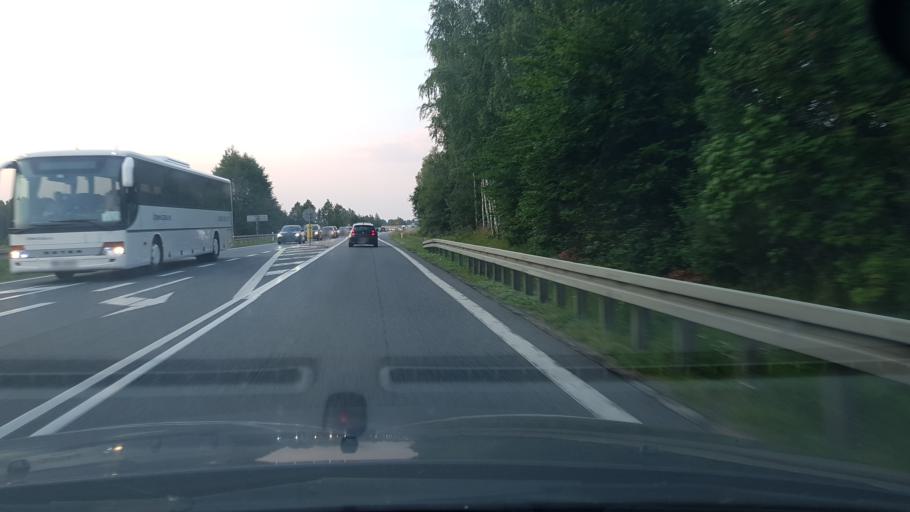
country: PL
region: Masovian Voivodeship
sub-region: Powiat mlawski
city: Wieczfnia Koscielna
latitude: 53.1873
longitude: 20.4312
